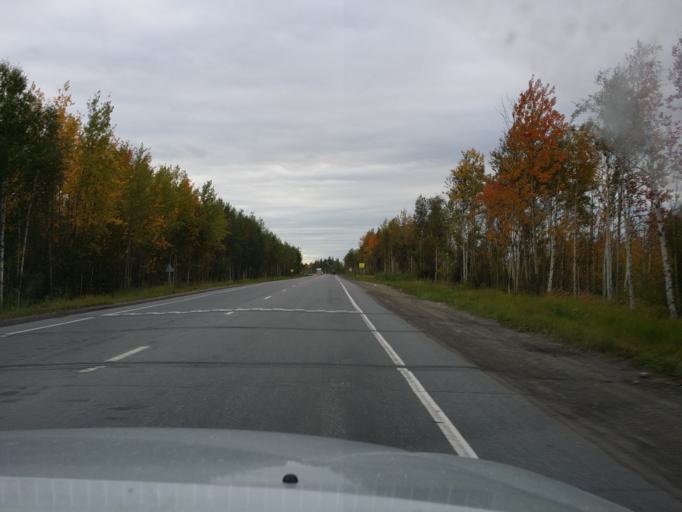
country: RU
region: Khanty-Mansiyskiy Avtonomnyy Okrug
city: Megion
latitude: 61.0684
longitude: 76.2287
